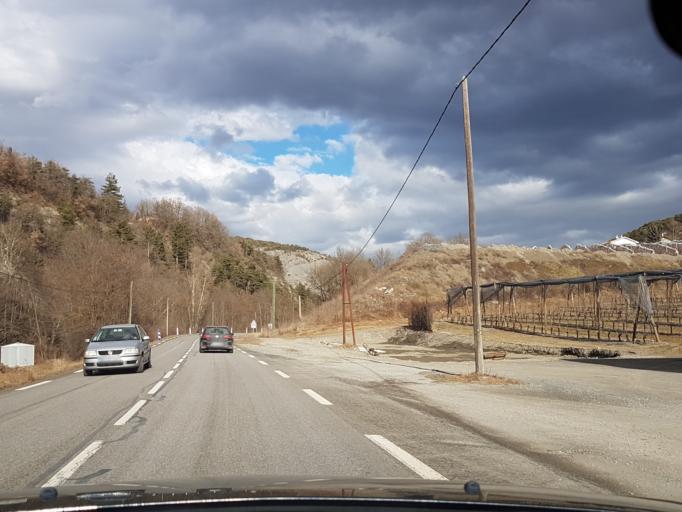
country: FR
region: Provence-Alpes-Cote d'Azur
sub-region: Departement des Hautes-Alpes
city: Tallard
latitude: 44.4835
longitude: 6.0794
